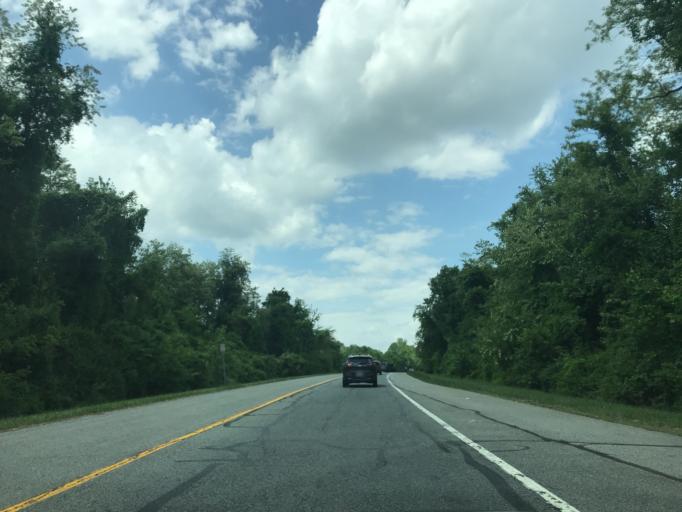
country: US
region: Maryland
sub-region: Harford County
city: North Bel Air
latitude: 39.5372
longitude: -76.3673
